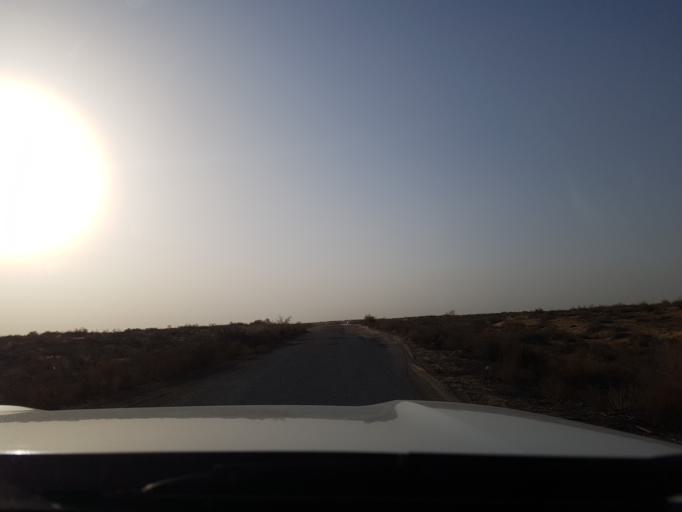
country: UZ
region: Xorazm
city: Hazorasp
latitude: 41.1739
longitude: 60.8239
